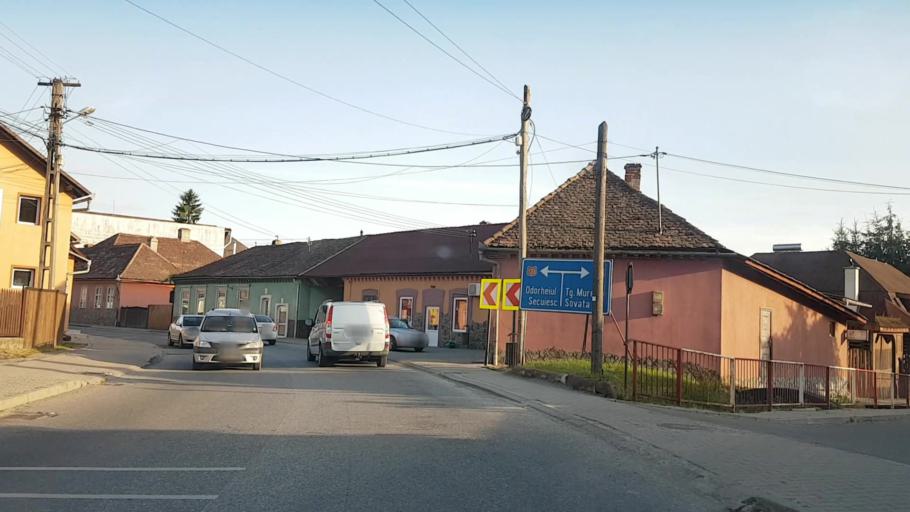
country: RO
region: Harghita
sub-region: Comuna Praid
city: Praid
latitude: 46.5525
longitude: 25.1263
